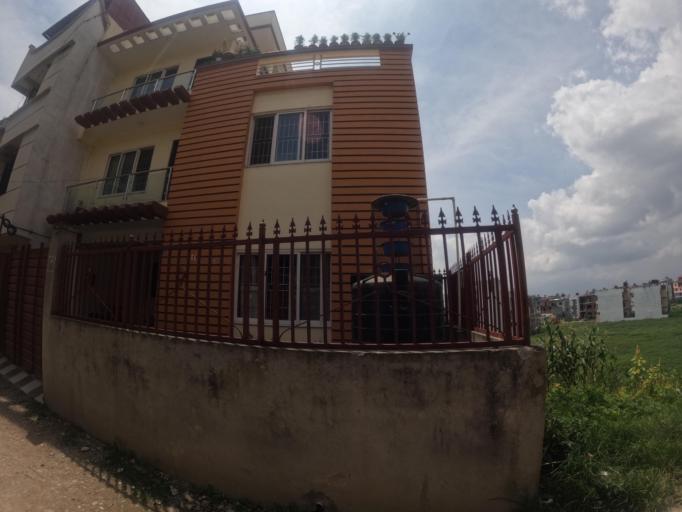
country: NP
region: Central Region
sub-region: Bagmati Zone
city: Kathmandu
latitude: 27.6796
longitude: 85.3692
